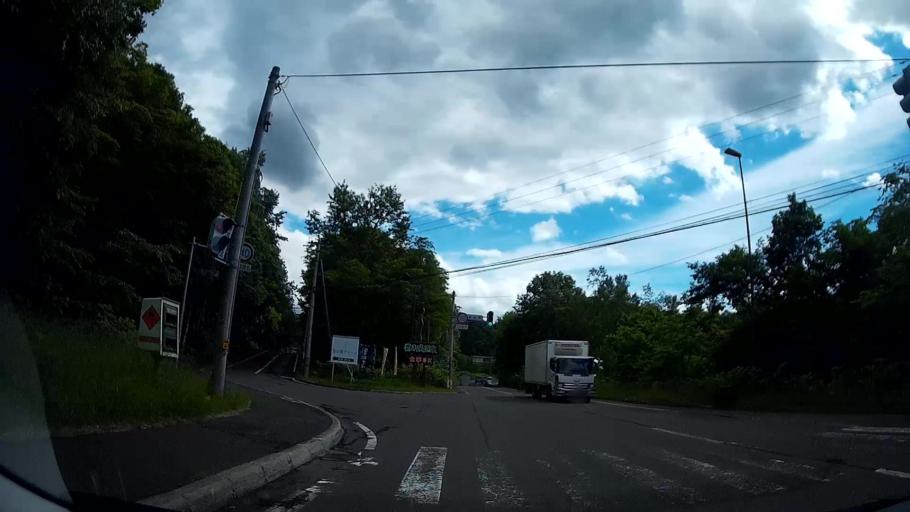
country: JP
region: Hokkaido
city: Sapporo
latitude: 42.9543
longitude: 141.1517
